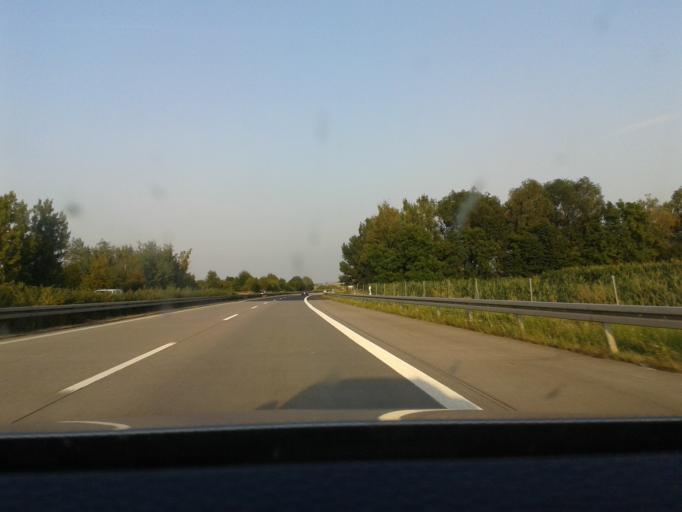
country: DE
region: Saxony
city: Grossweitzschen
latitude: 51.1678
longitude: 13.0792
